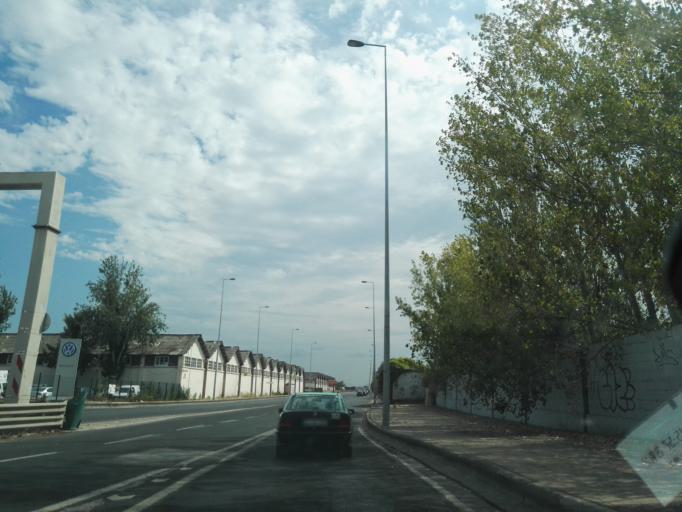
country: PT
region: Lisbon
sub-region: Loures
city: Moscavide
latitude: 38.7523
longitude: -9.0958
